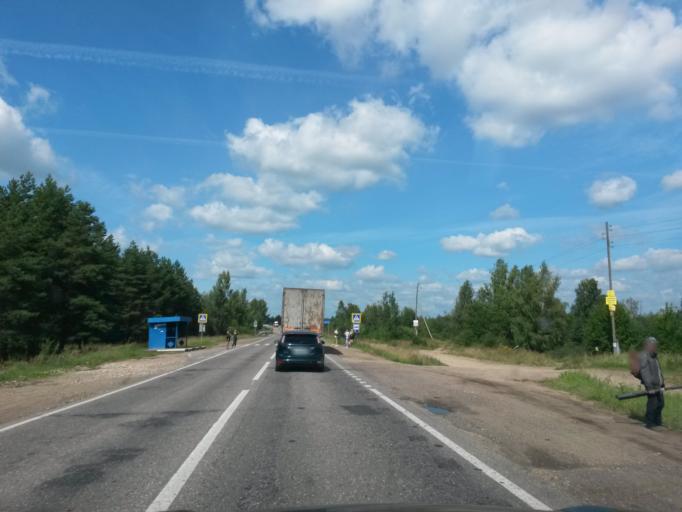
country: RU
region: Jaroslavl
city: Yaroslavl
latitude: 57.5093
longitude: 39.8978
